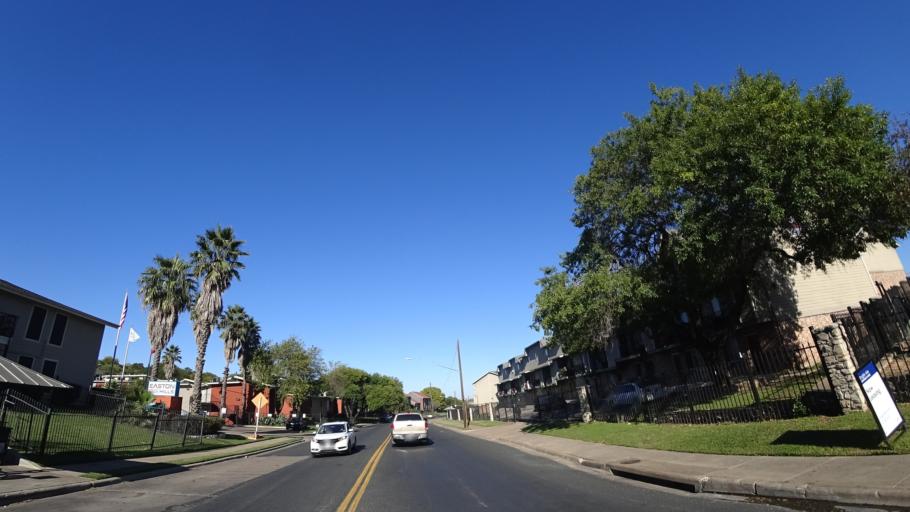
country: US
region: Texas
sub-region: Travis County
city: Austin
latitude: 30.2338
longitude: -97.7318
